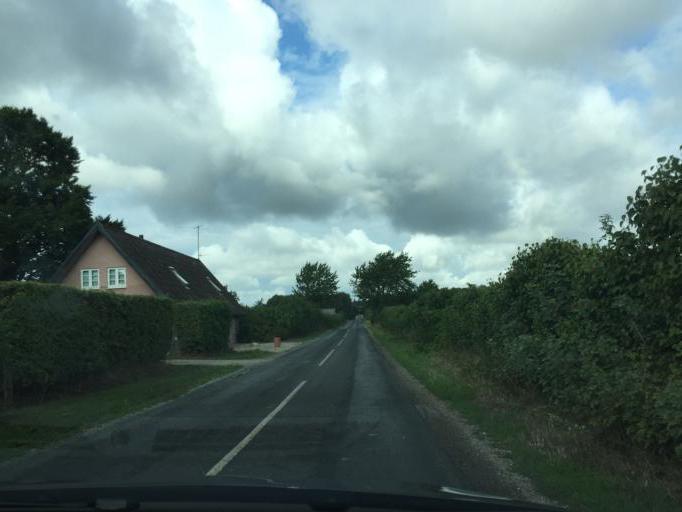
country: DK
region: South Denmark
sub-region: Assens Kommune
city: Harby
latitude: 55.1939
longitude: 10.2161
